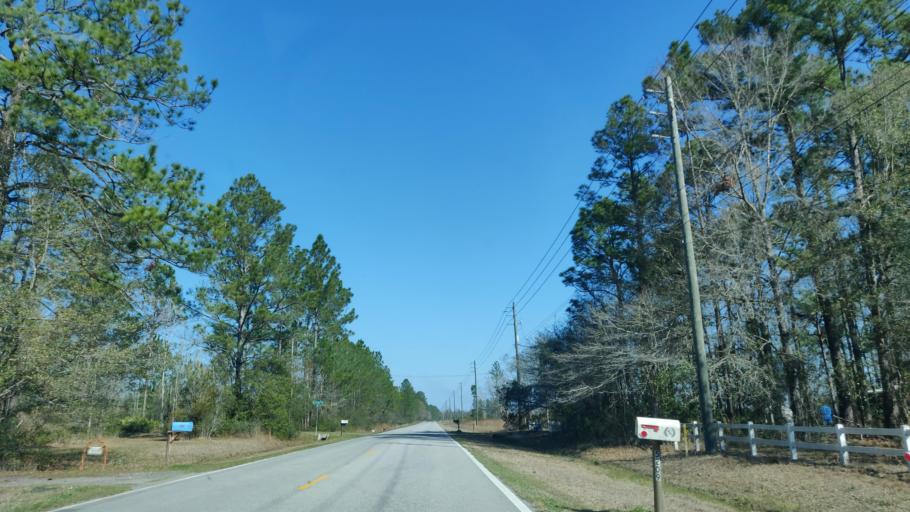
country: US
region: Florida
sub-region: Duval County
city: Baldwin
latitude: 30.2226
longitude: -81.9410
